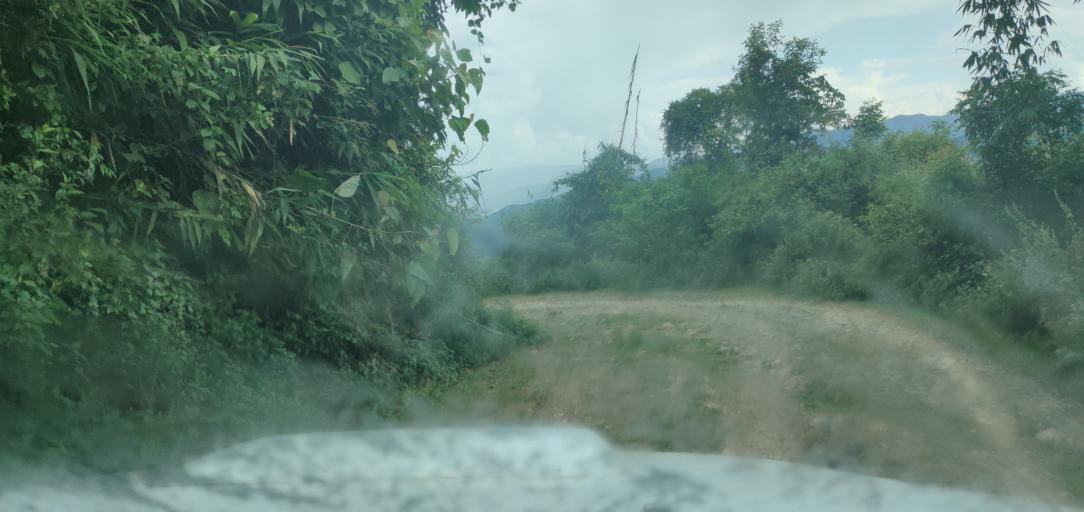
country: LA
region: Phongsali
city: Phongsali
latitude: 21.4468
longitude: 102.3123
